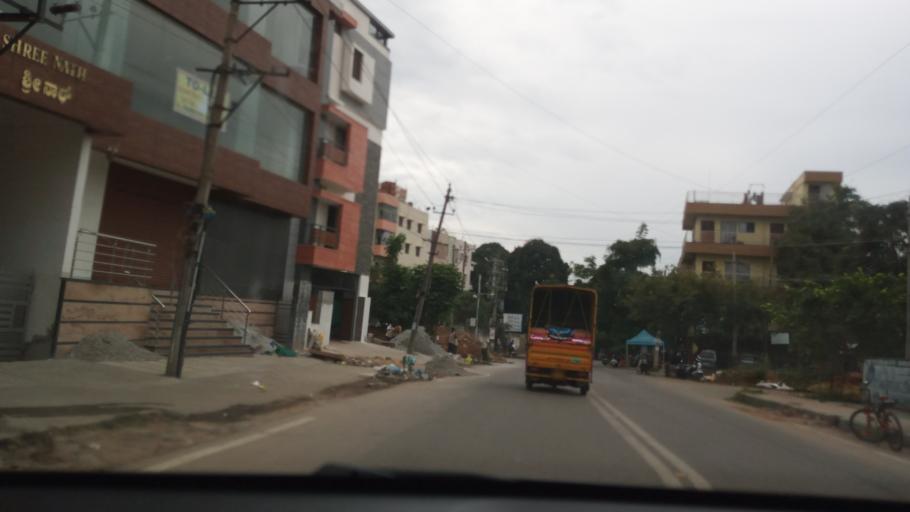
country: IN
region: Karnataka
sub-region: Bangalore Urban
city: Bangalore
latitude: 13.0149
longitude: 77.5389
